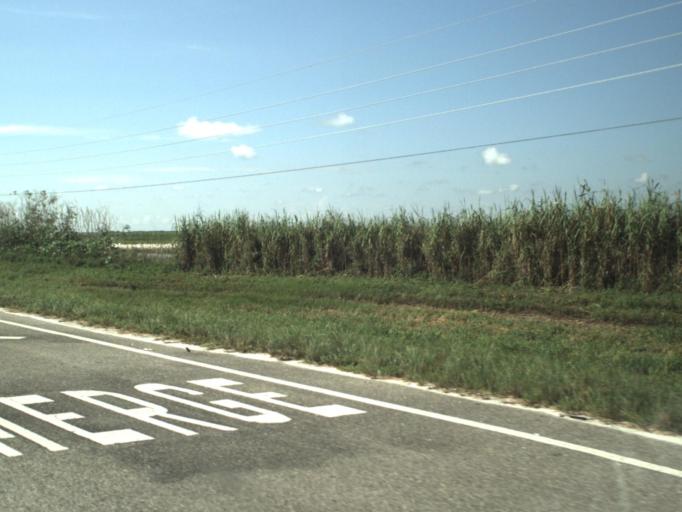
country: US
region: Florida
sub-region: Palm Beach County
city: Belle Glade Camp
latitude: 26.4530
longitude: -80.6295
